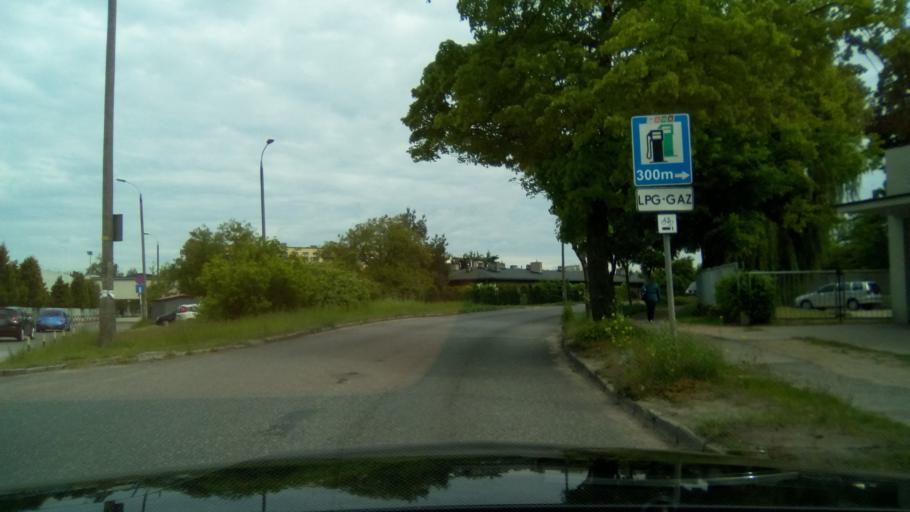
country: PL
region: Greater Poland Voivodeship
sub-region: Powiat gnieznienski
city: Gniezno
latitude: 52.5183
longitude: 17.5997
